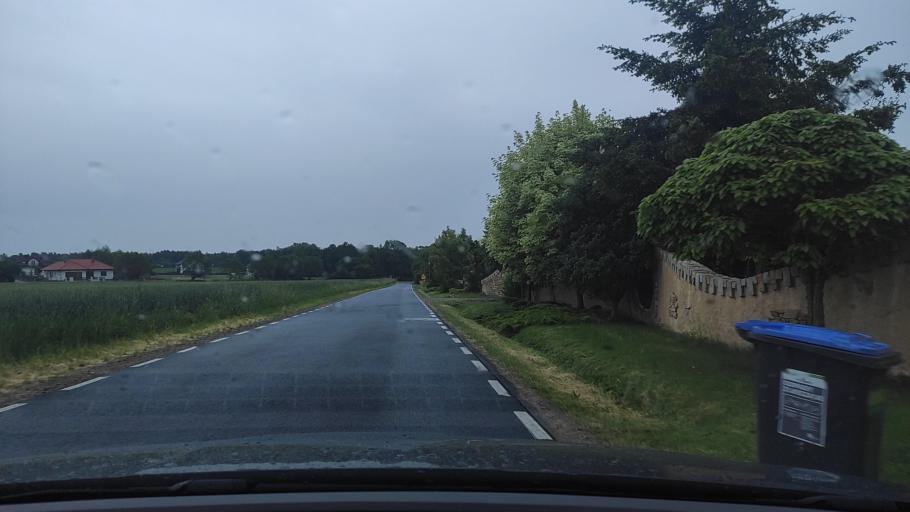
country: PL
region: Greater Poland Voivodeship
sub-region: Powiat poznanski
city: Kostrzyn
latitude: 52.4806
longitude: 17.1742
